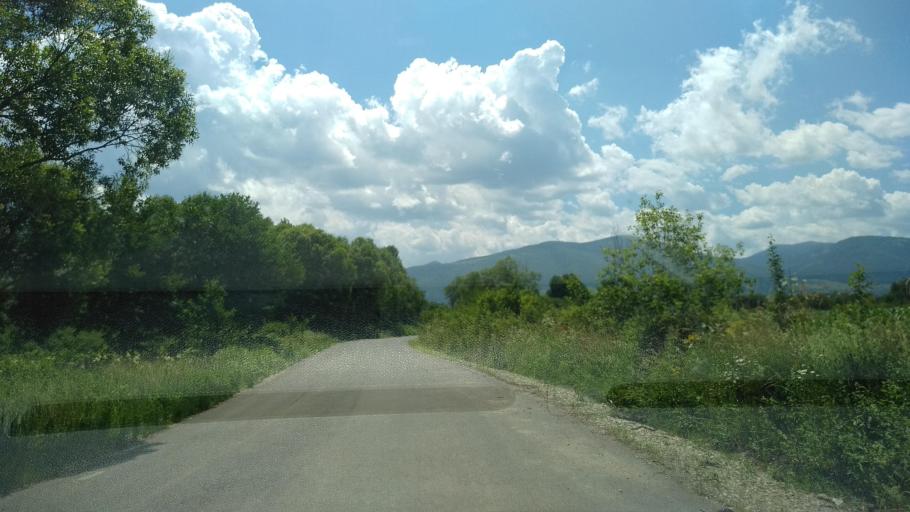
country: RO
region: Hunedoara
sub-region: Comuna Sarmizegetusa
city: Sarmizegetusa
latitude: 45.5351
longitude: 22.8184
